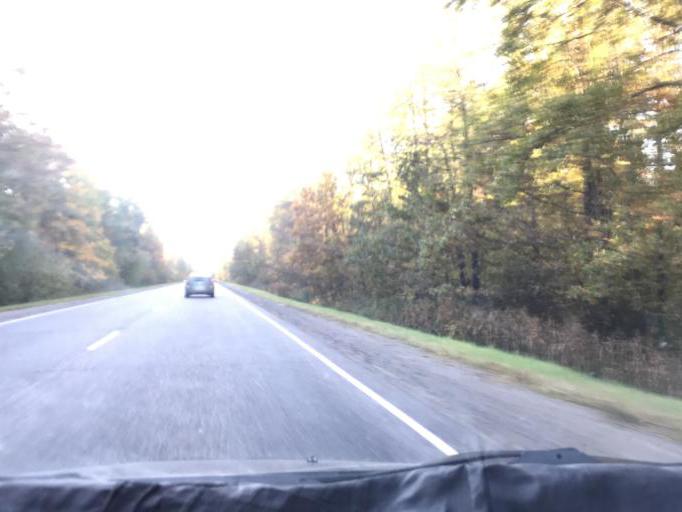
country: BY
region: Gomel
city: Pyetrykaw
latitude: 52.2627
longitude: 28.3171
